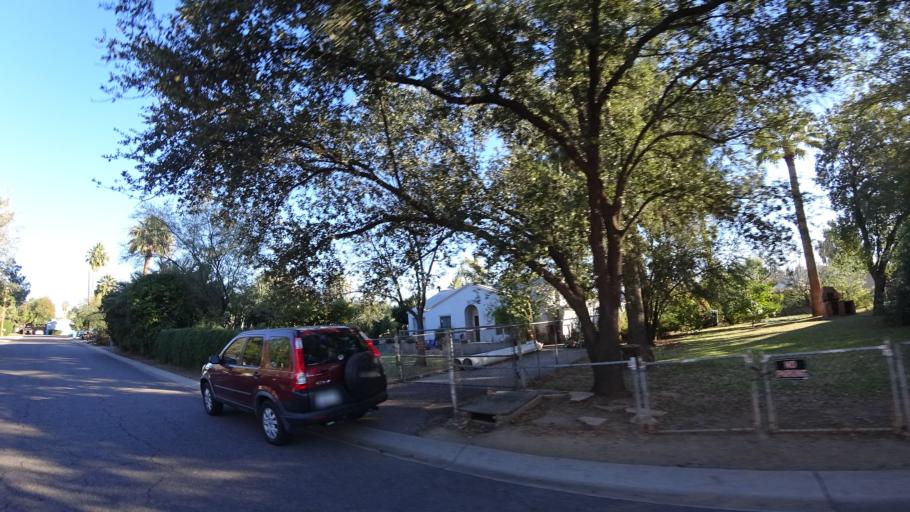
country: US
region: Arizona
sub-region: Maricopa County
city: Phoenix
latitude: 33.4910
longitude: -112.0512
